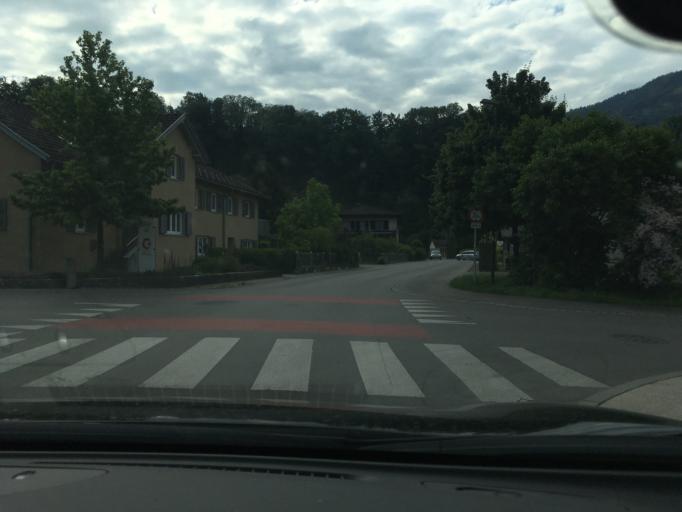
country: AT
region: Vorarlberg
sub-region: Politischer Bezirk Feldkirch
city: Nofels
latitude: 47.2369
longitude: 9.5786
